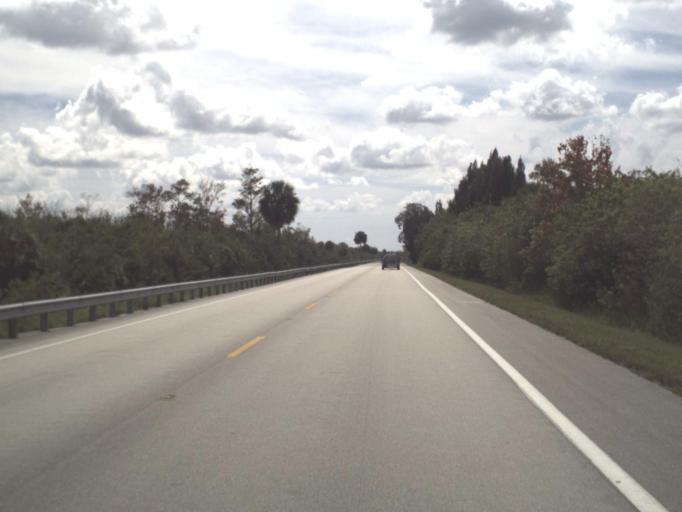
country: US
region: Florida
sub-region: Collier County
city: Lely Resort
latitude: 25.9347
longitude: -81.3573
